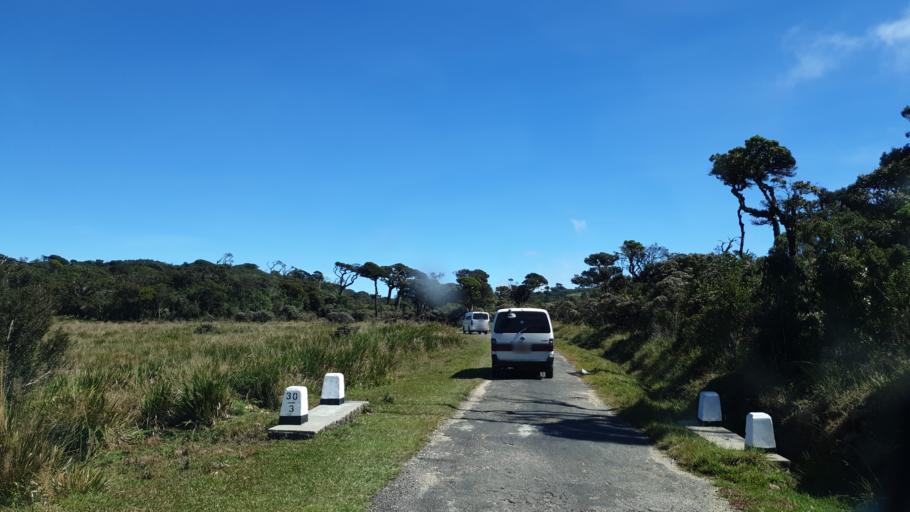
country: LK
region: Uva
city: Haputale
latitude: 6.7953
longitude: 80.8285
